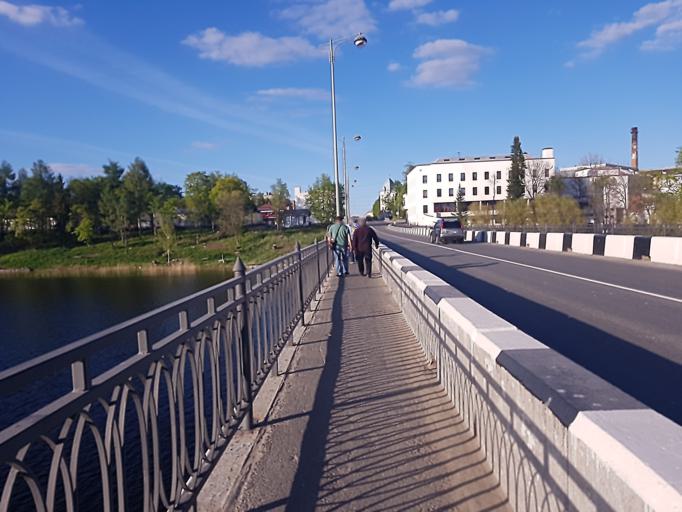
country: RU
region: Republic of Karelia
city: Sortavala
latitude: 61.7005
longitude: 30.6857
